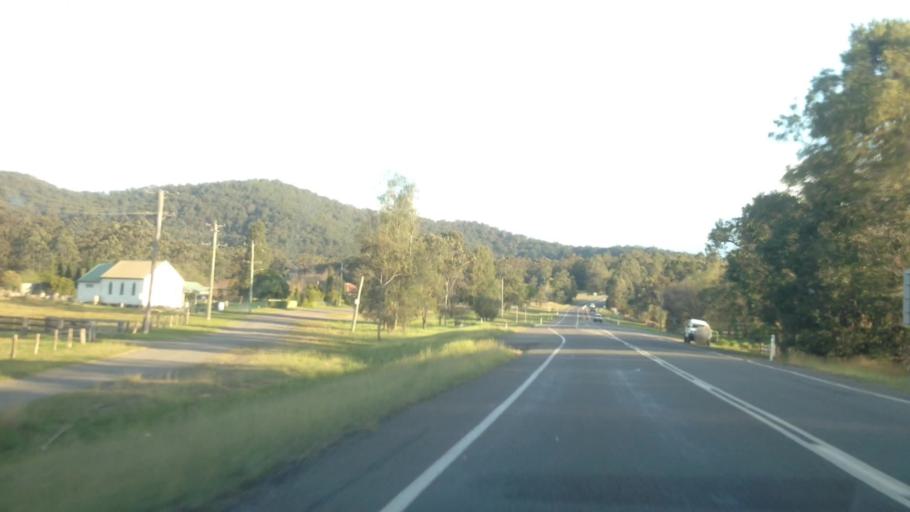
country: AU
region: New South Wales
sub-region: Lake Macquarie Shire
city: Holmesville
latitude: -32.9509
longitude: 151.4794
